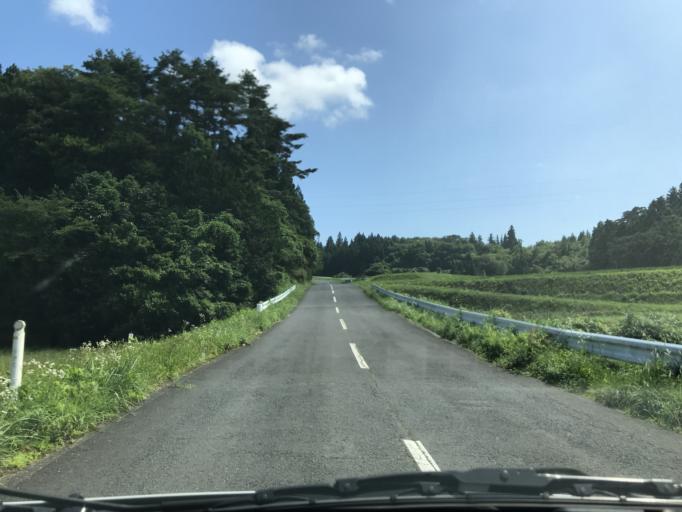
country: JP
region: Iwate
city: Ofunato
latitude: 39.0046
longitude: 141.4252
